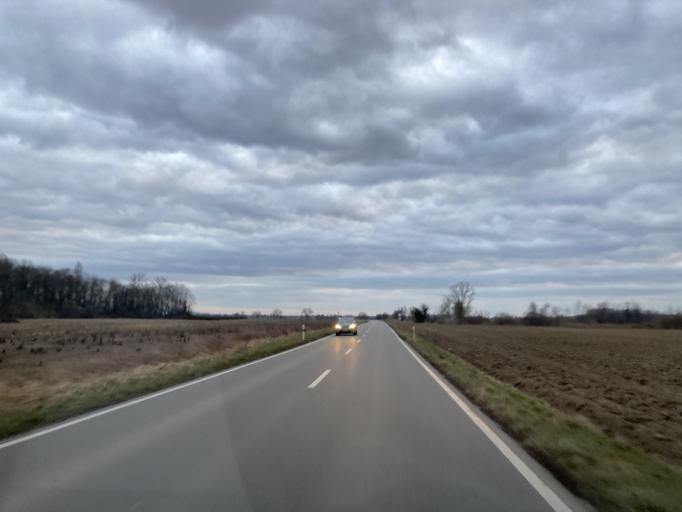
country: DE
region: Baden-Wuerttemberg
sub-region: Freiburg Region
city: Breisach am Rhein
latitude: 48.0710
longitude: 7.5948
